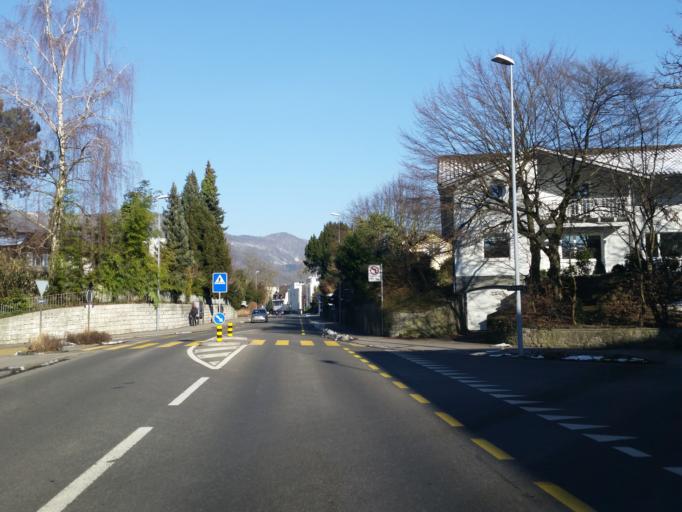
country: CH
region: Aargau
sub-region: Bezirk Baden
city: Wettingen
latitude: 47.4606
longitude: 8.3184
